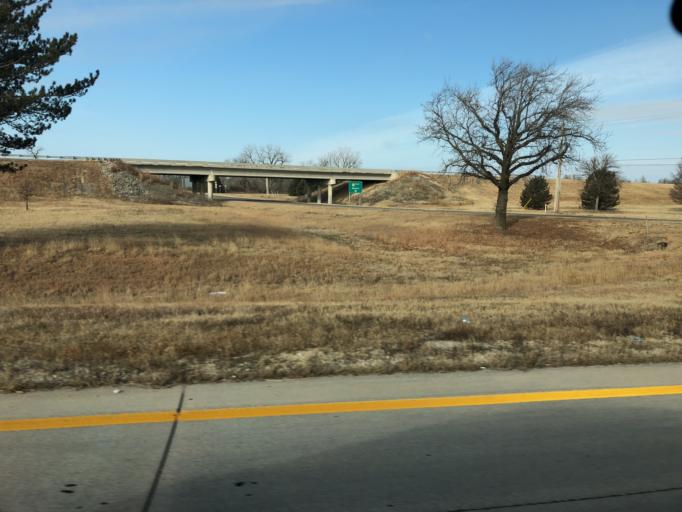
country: US
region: Kansas
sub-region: Reno County
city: South Hutchinson
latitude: 38.0568
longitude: -97.9847
